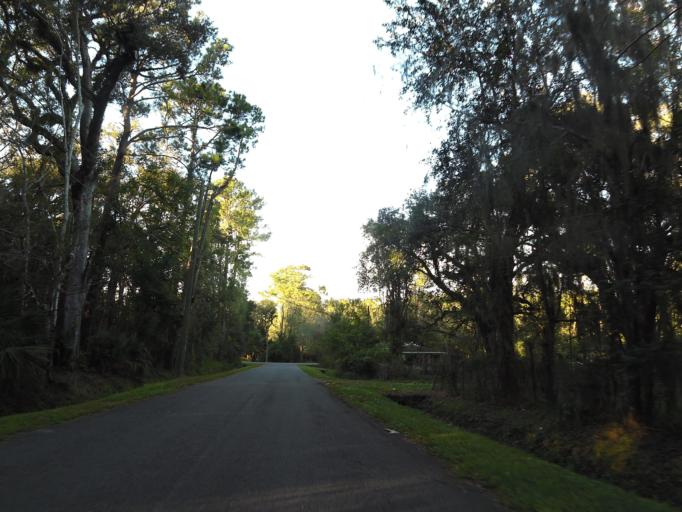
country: US
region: Florida
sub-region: Duval County
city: Jacksonville
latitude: 30.3248
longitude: -81.7721
